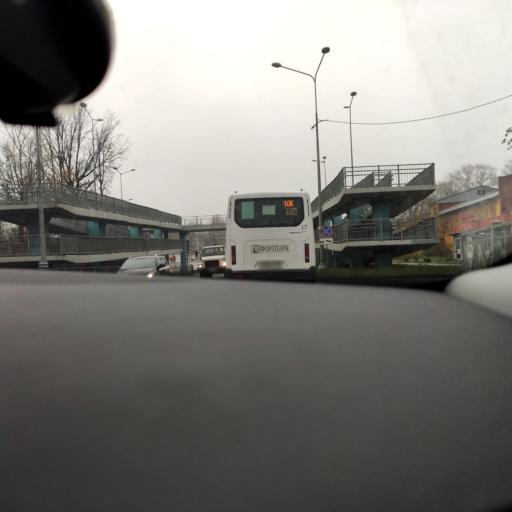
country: RU
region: Moskovskaya
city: Nakhabino
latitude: 55.8396
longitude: 37.1637
